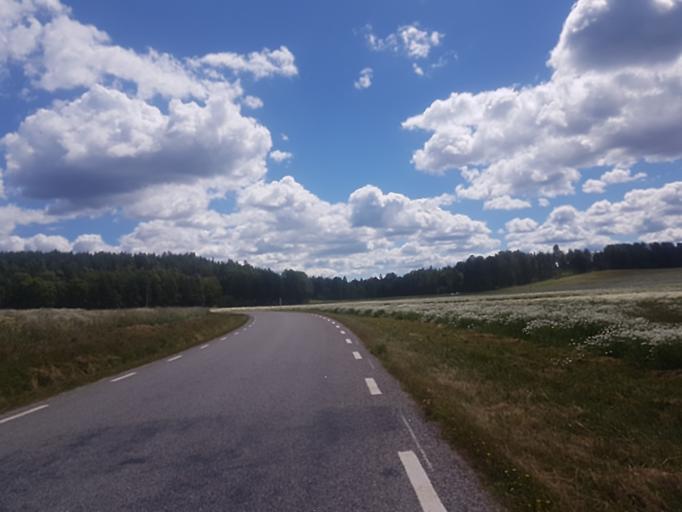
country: SE
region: Soedermanland
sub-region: Gnesta Kommun
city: Gnesta
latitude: 59.0414
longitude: 17.3434
